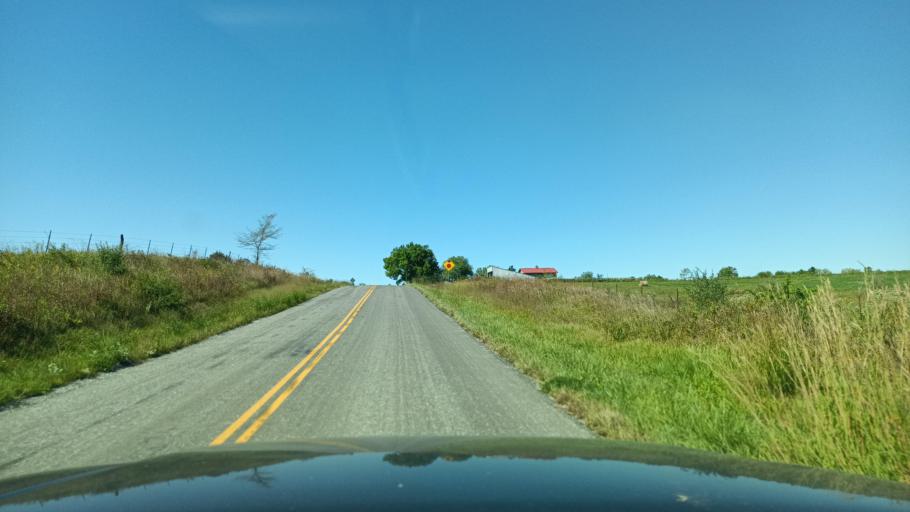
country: US
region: Missouri
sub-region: Adair County
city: Kirksville
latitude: 40.3298
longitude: -92.5591
